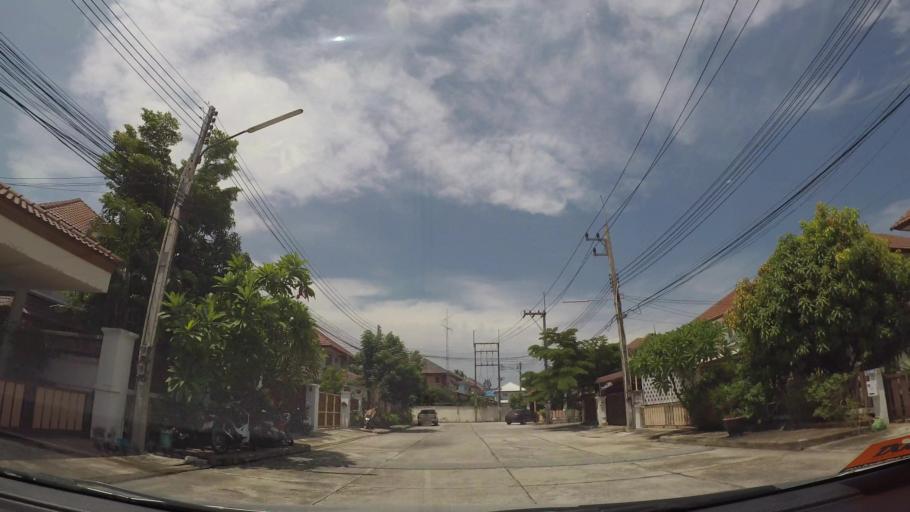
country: TH
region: Chon Buri
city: Chon Buri
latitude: 13.3255
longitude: 100.9456
